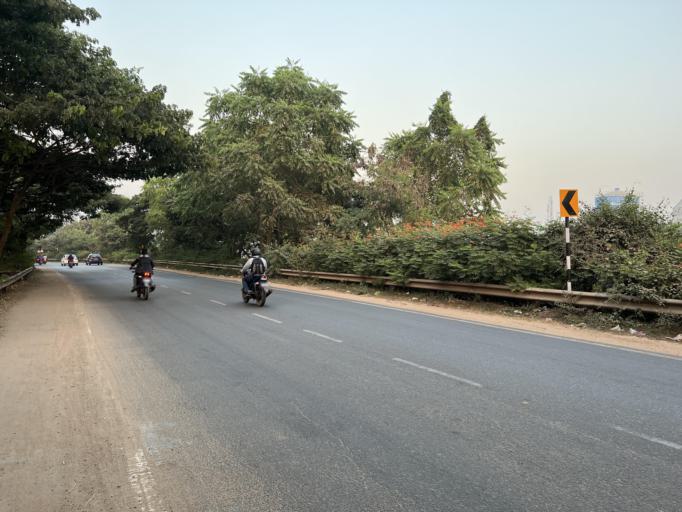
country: IN
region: Odisha
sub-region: Khordha
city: Bhubaneshwar
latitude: 20.3151
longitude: 85.8779
